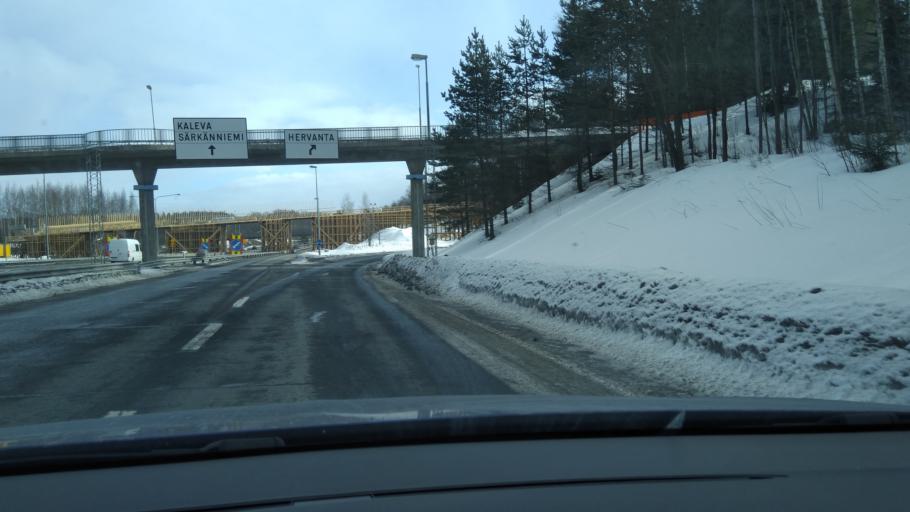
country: FI
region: Pirkanmaa
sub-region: Tampere
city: Tampere
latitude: 61.4699
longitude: 23.8338
